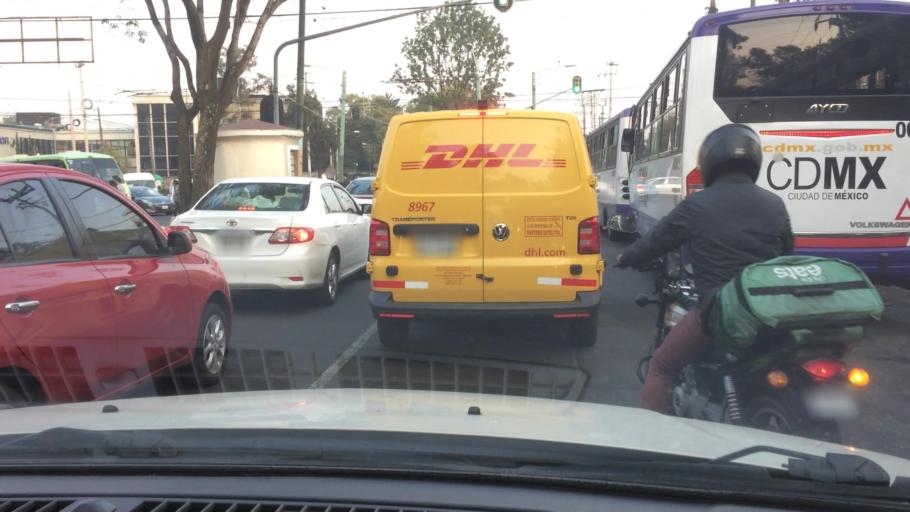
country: MX
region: Mexico City
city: Coyoacan
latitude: 19.3471
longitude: -99.1812
